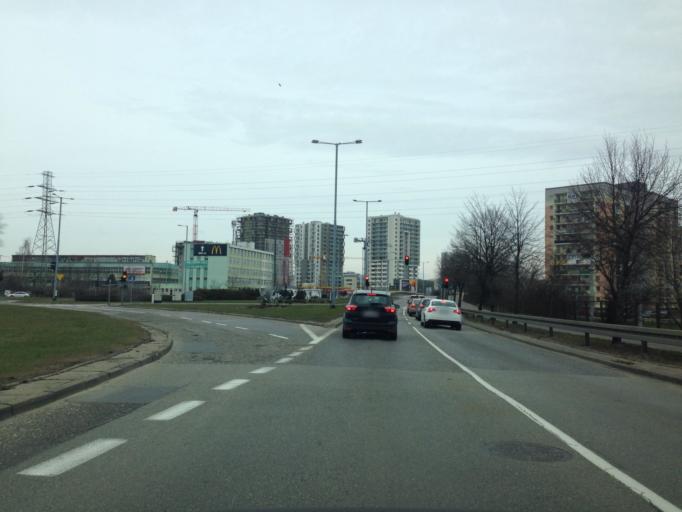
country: PL
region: Pomeranian Voivodeship
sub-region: Sopot
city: Sopot
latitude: 54.3989
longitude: 18.5949
